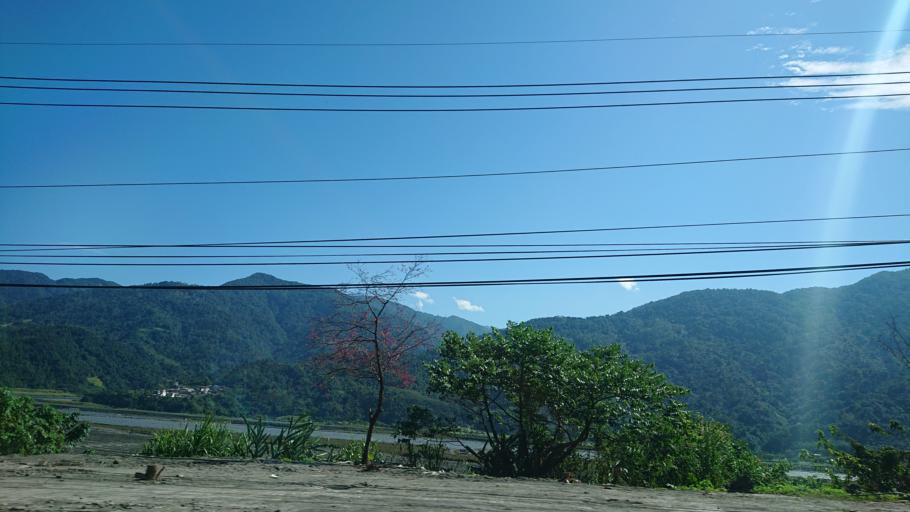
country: TW
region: Taiwan
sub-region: Yilan
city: Yilan
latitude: 24.6014
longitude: 121.5150
